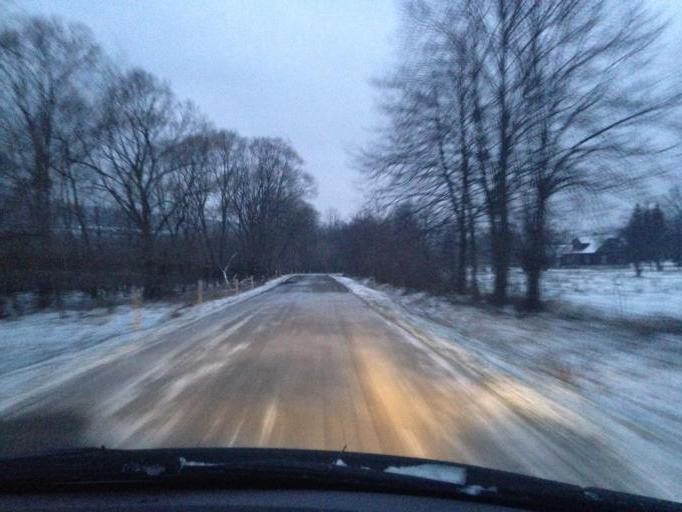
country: PL
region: Subcarpathian Voivodeship
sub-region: Powiat jasielski
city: Krempna
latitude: 49.5296
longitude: 21.5537
